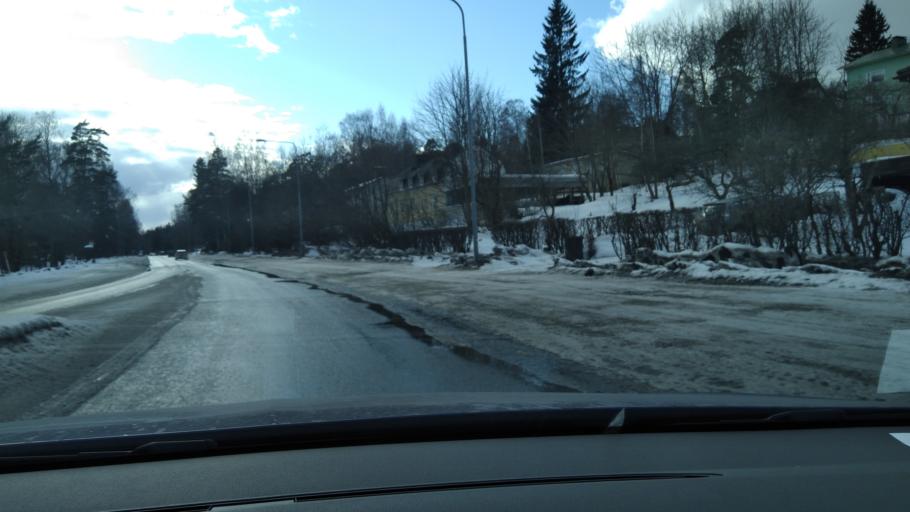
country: FI
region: Pirkanmaa
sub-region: Tampere
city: Pirkkala
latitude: 61.5008
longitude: 23.6463
